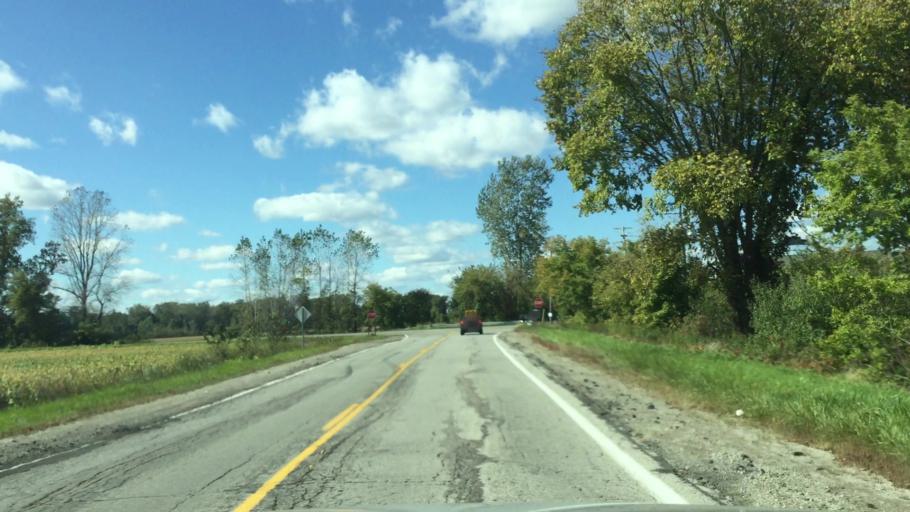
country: US
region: Michigan
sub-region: Genesee County
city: Swartz Creek
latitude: 42.9418
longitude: -83.8572
